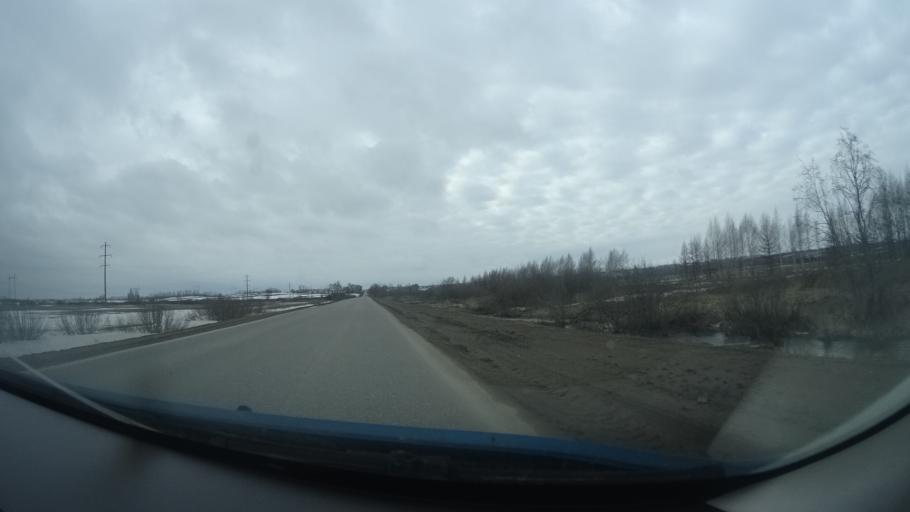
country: RU
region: Bashkortostan
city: Birsk
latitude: 55.4630
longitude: 55.5935
